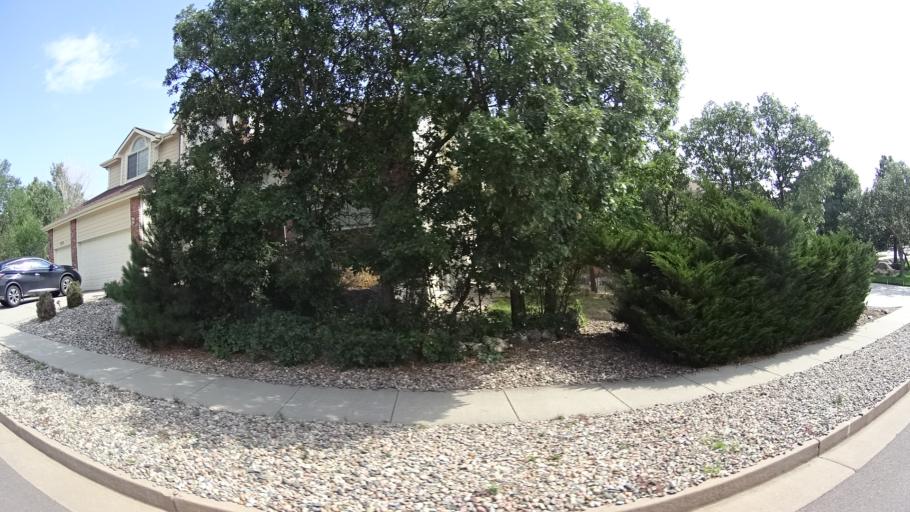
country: US
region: Colorado
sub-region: El Paso County
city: Fort Carson
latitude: 38.7453
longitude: -104.8324
